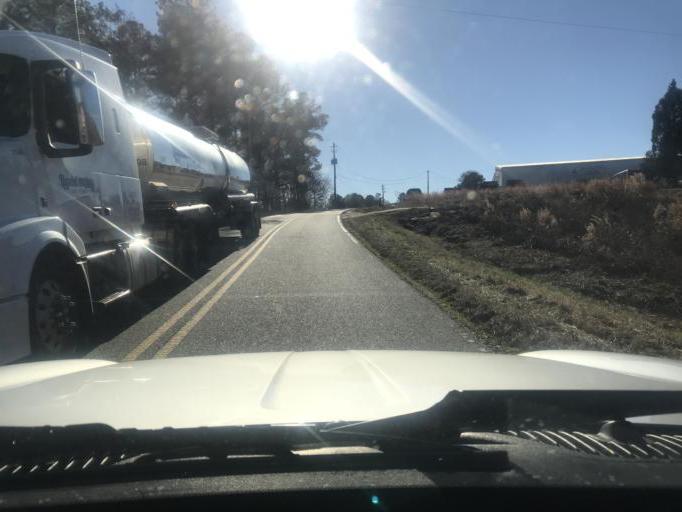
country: US
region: Georgia
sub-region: Barrow County
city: Winder
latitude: 33.9972
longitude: -83.7598
